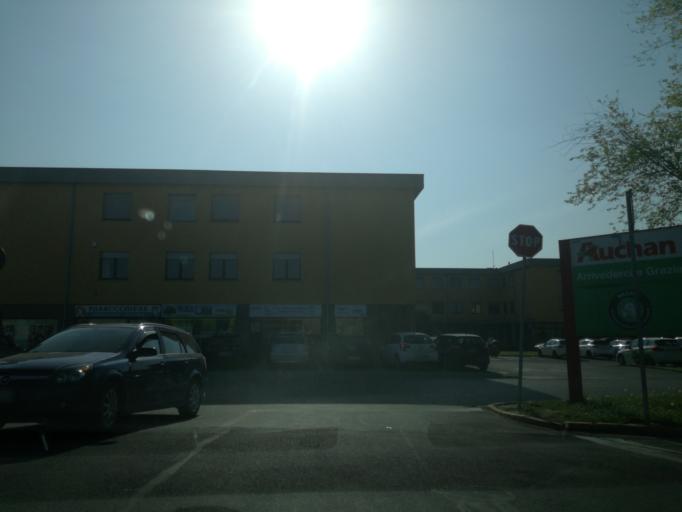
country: IT
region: Lombardy
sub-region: Provincia di Lecco
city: Merate
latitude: 45.6891
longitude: 9.4210
